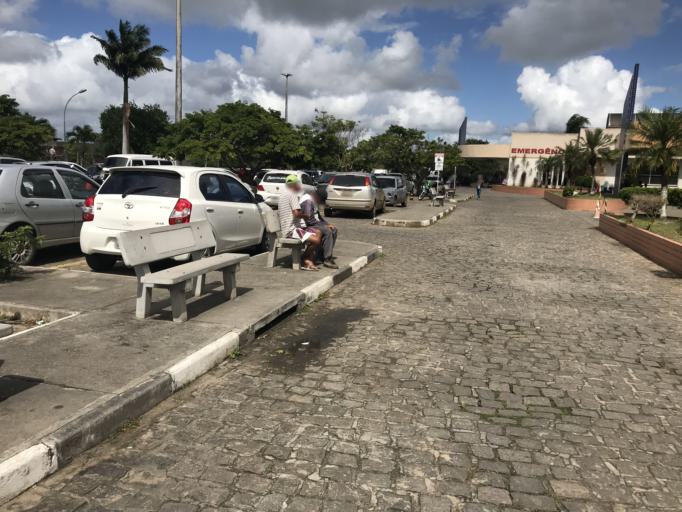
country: BR
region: Bahia
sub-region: Santo Antonio De Jesus
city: Santo Antonio de Jesus
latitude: -12.9806
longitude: -39.2809
